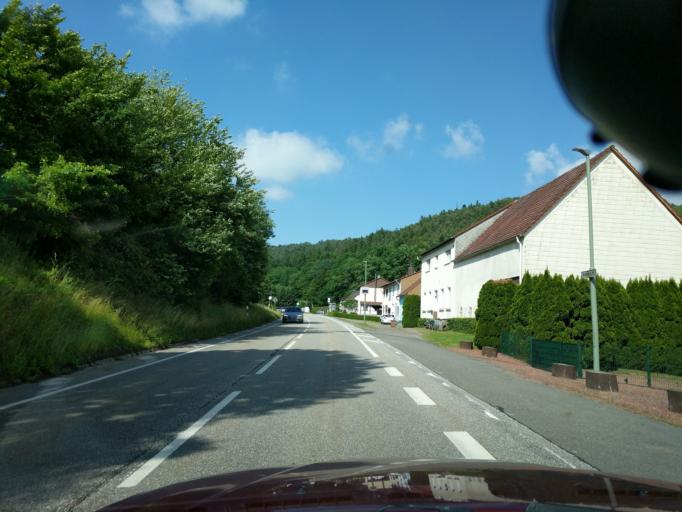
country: DE
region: Rheinland-Pfalz
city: Stelzenberg
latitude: 49.3974
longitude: 7.7116
